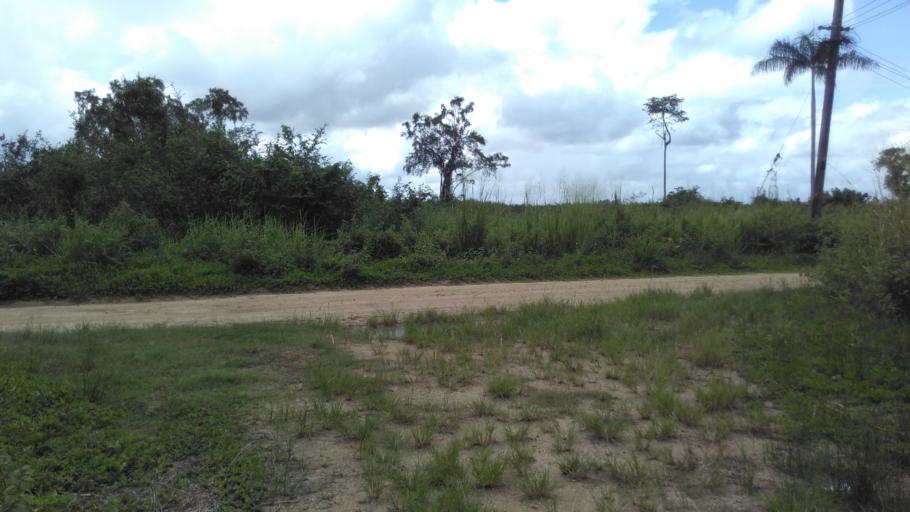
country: SR
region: Paramaribo
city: Paramaribo
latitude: 5.7735
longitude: -55.1308
